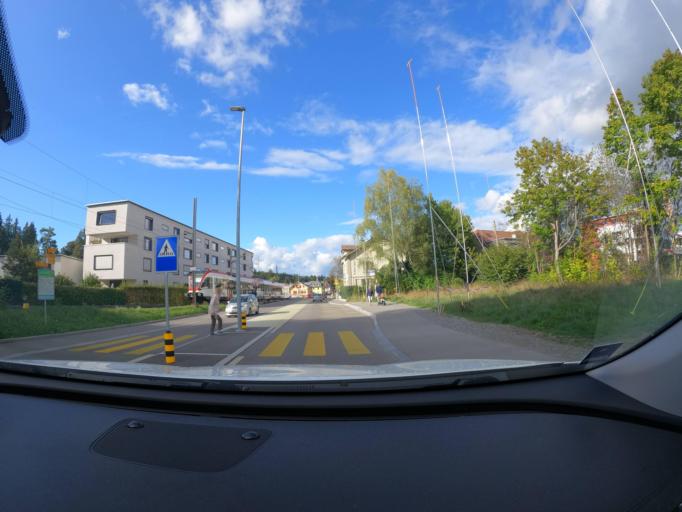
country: CH
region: Aargau
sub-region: Bezirk Lenzburg
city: Seon
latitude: 47.3469
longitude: 8.1590
